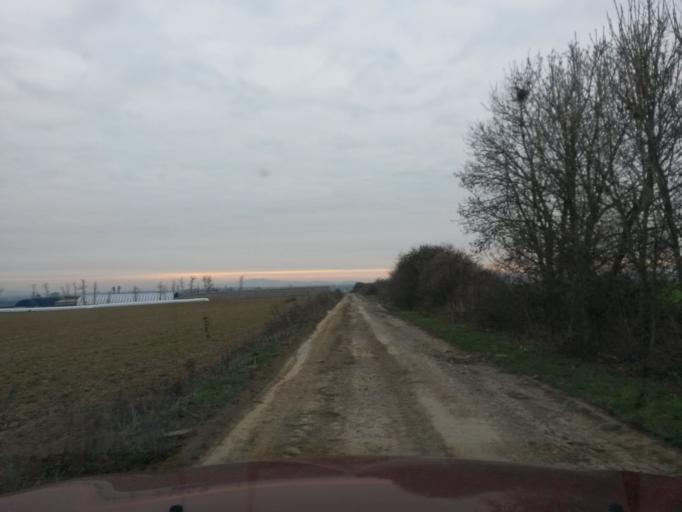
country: SK
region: Kosicky
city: Secovce
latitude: 48.6613
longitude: 21.6693
